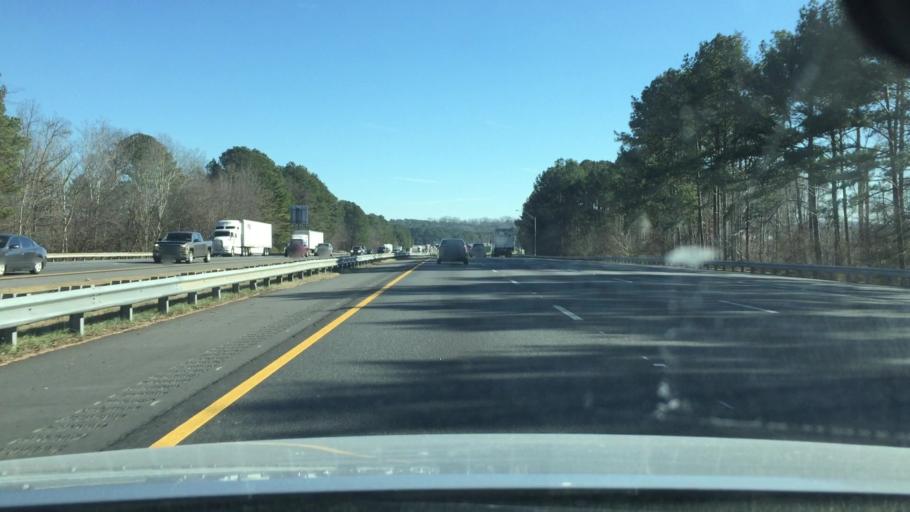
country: US
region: Georgia
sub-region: Catoosa County
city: Ringgold
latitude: 34.8849
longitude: -85.0597
